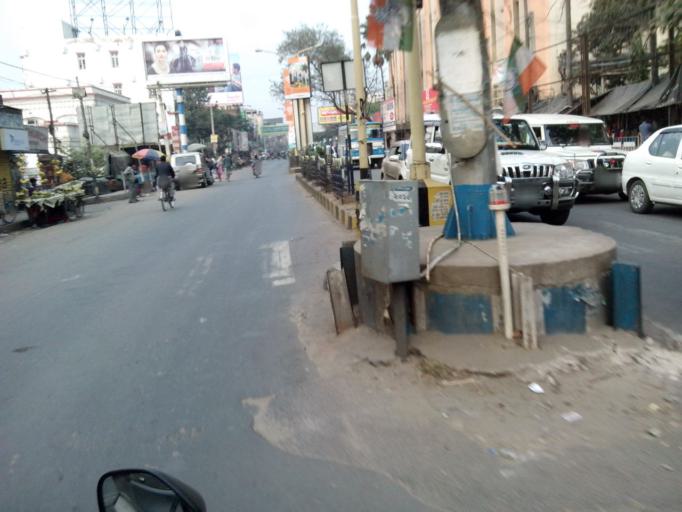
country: IN
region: West Bengal
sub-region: Barddhaman
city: Barddhaman
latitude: 23.2373
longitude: 87.8665
